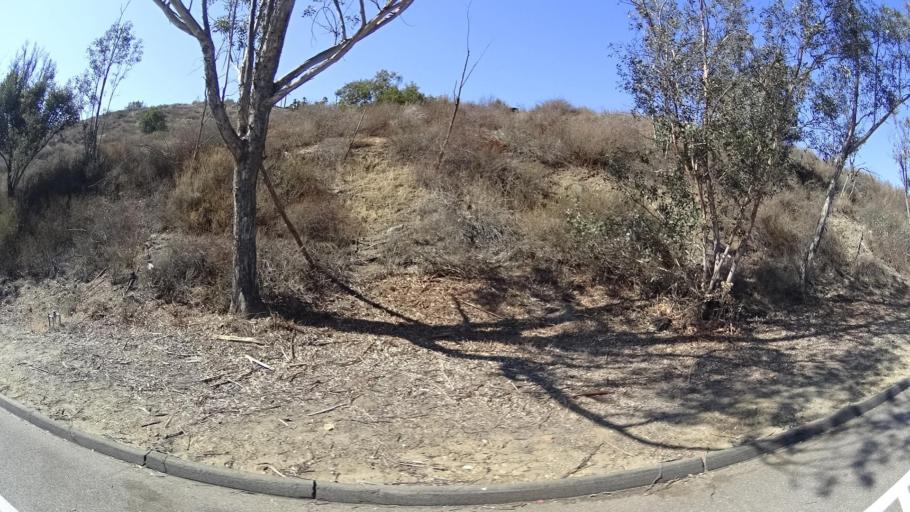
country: US
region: California
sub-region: San Diego County
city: Hidden Meadows
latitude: 33.2555
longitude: -117.1497
